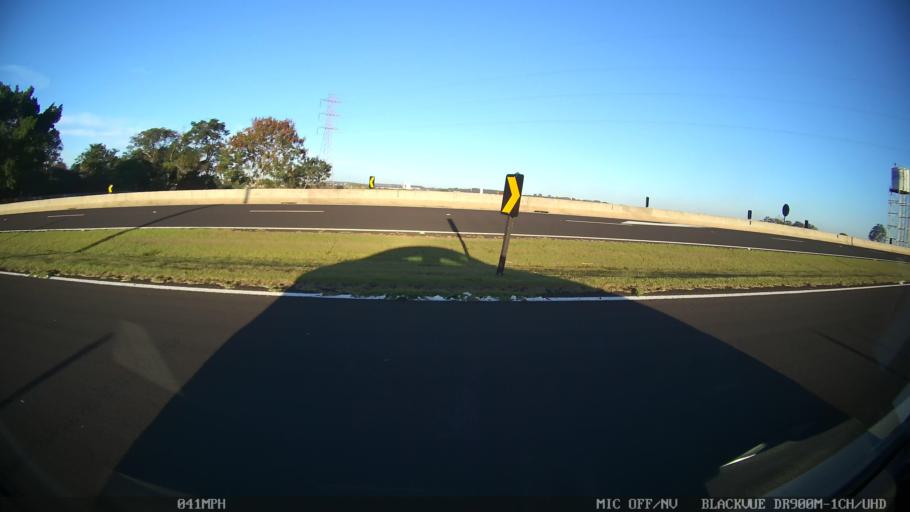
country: BR
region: Sao Paulo
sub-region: Araraquara
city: Araraquara
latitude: -21.8088
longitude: -48.1961
